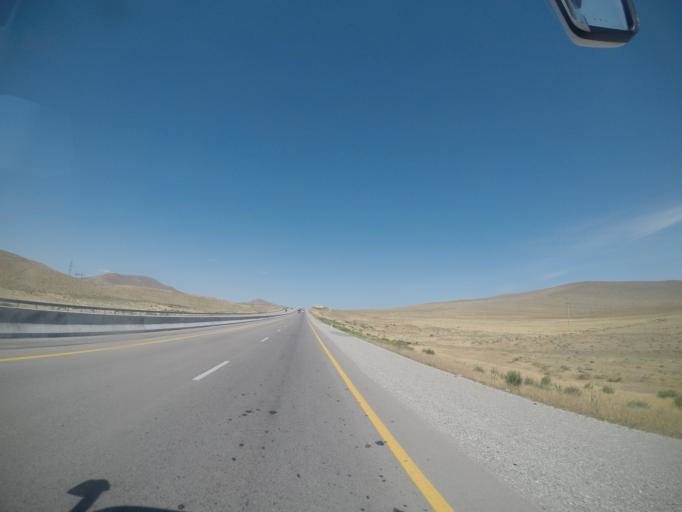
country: AZ
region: Sumqayit
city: Haci Zeynalabdin
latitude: 40.4983
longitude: 49.3042
